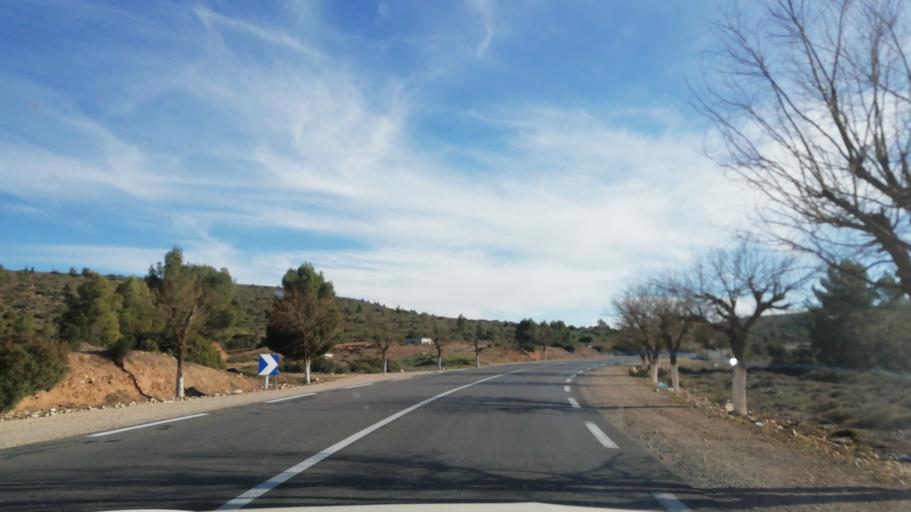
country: DZ
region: Tlemcen
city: Sebdou
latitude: 34.6019
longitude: -1.3243
